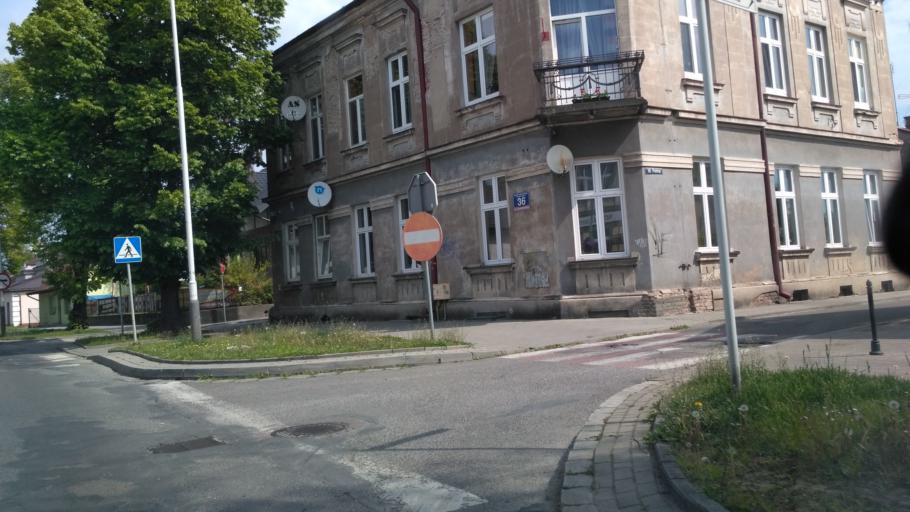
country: PL
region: Subcarpathian Voivodeship
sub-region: Powiat jaroslawski
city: Jaroslaw
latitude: 50.0201
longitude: 22.6764
